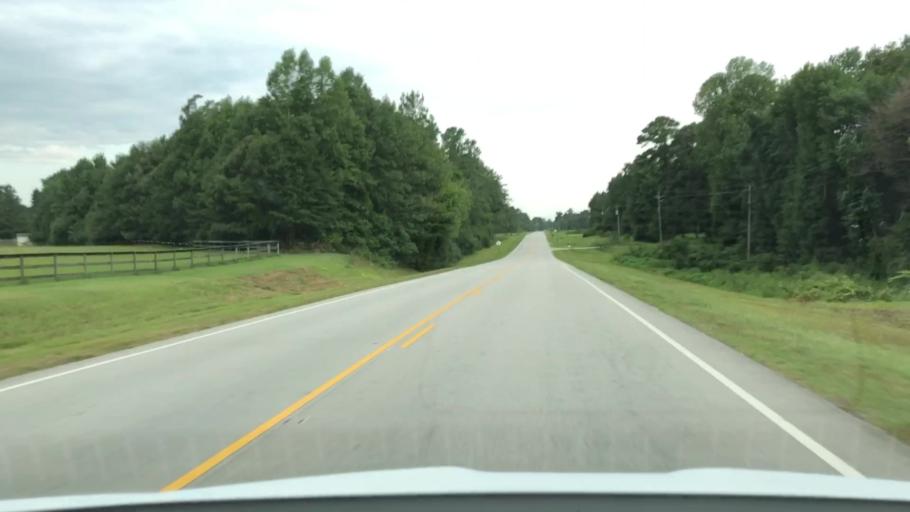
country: US
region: North Carolina
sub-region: Jones County
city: Trenton
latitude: 35.0118
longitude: -77.2902
